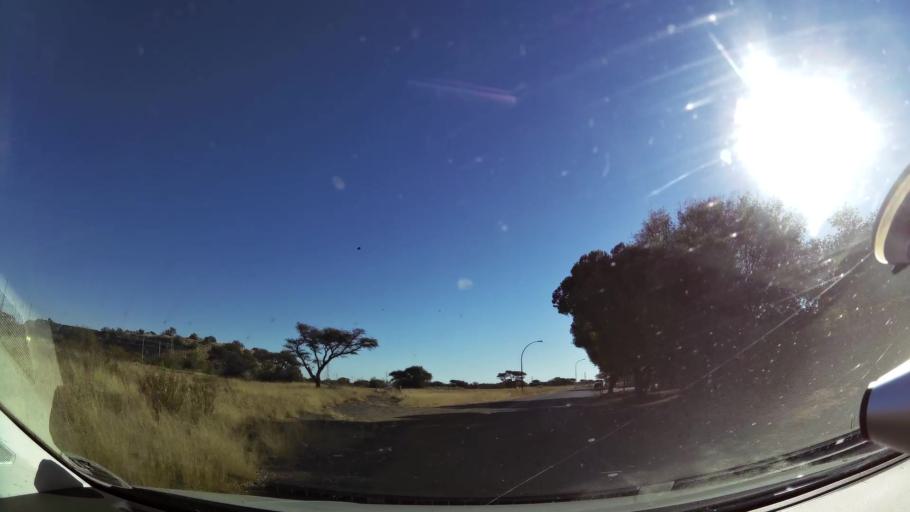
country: ZA
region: Northern Cape
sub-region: Frances Baard District Municipality
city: Kimberley
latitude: -28.7421
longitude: 24.7914
